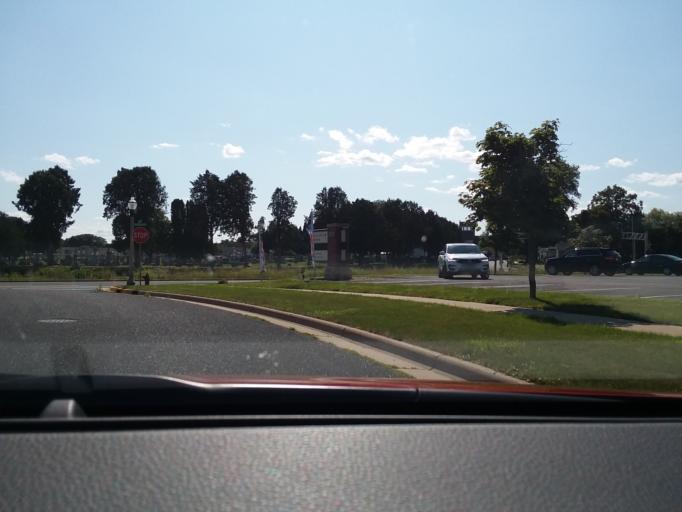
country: US
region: Wisconsin
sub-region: Dane County
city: Waunakee
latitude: 43.1897
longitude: -89.4504
